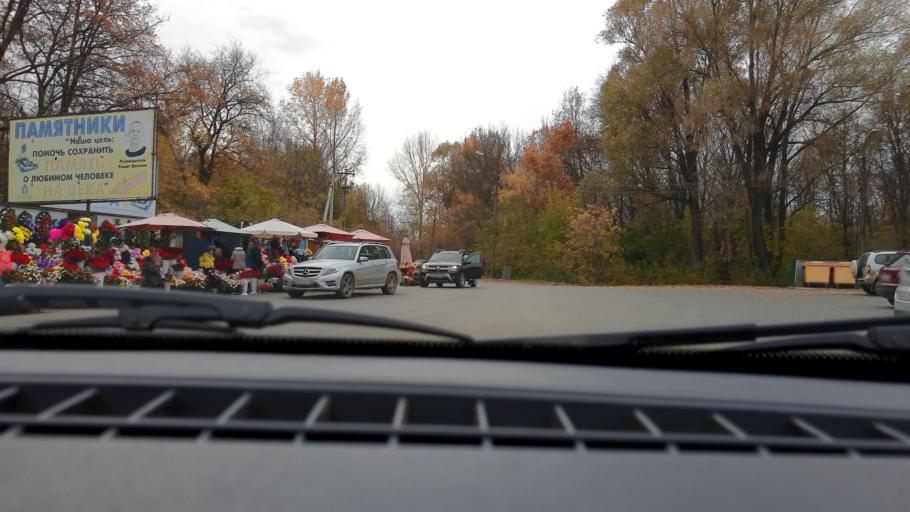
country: RU
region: Bashkortostan
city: Mikhaylovka
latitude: 54.8037
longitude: 55.8606
